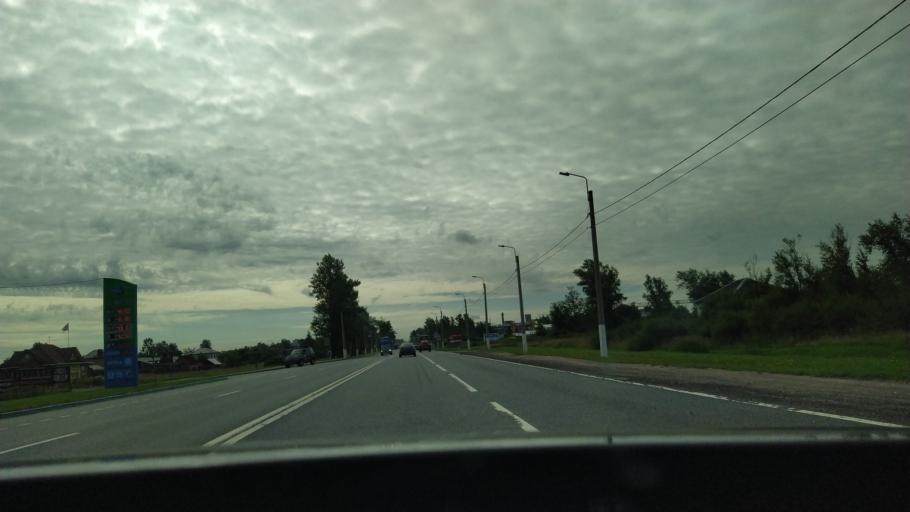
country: RU
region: Leningrad
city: Tosno
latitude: 59.5647
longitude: 30.8336
